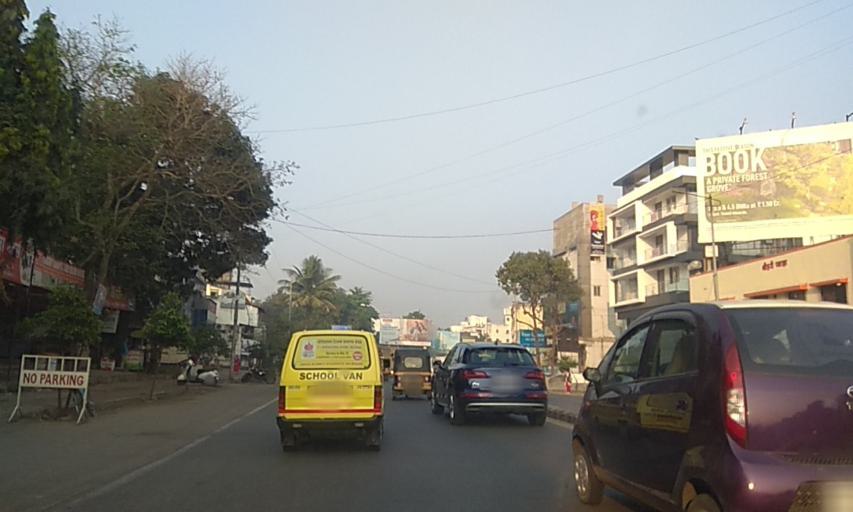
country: IN
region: Maharashtra
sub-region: Pune Division
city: Pimpri
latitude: 18.5615
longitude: 73.7855
